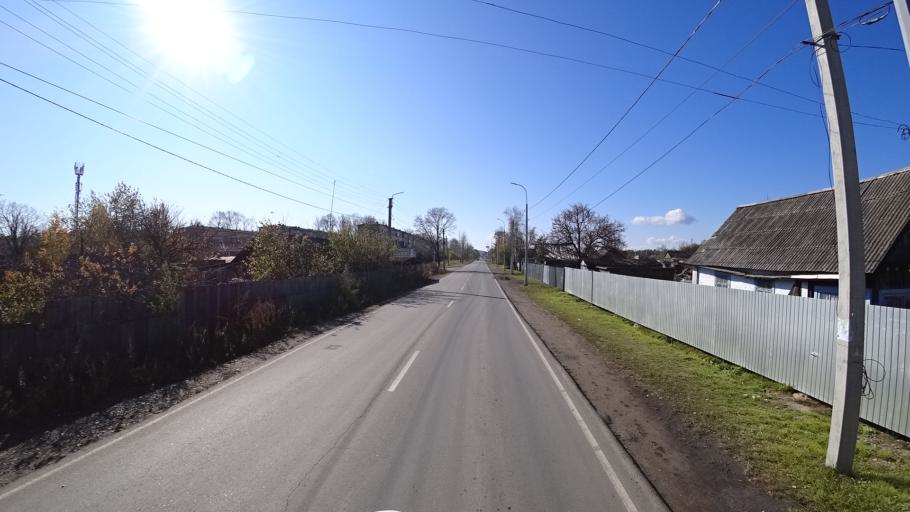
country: RU
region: Khabarovsk Krai
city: Amursk
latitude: 50.1019
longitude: 136.5106
